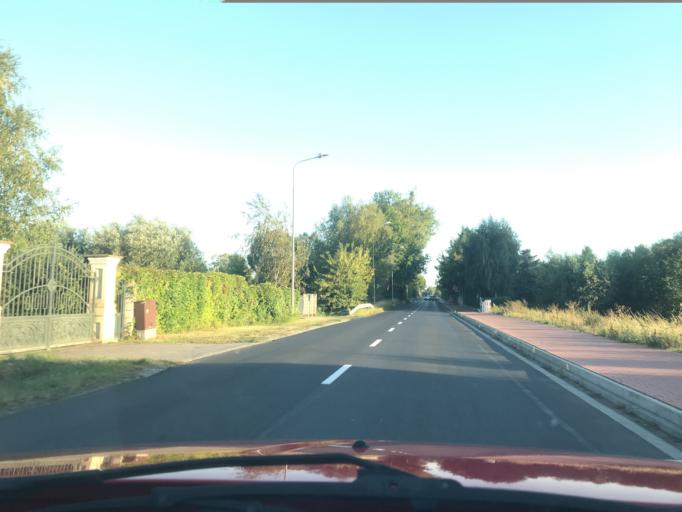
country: PL
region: Greater Poland Voivodeship
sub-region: Powiat poznanski
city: Baranowo
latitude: 52.4232
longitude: 16.7179
